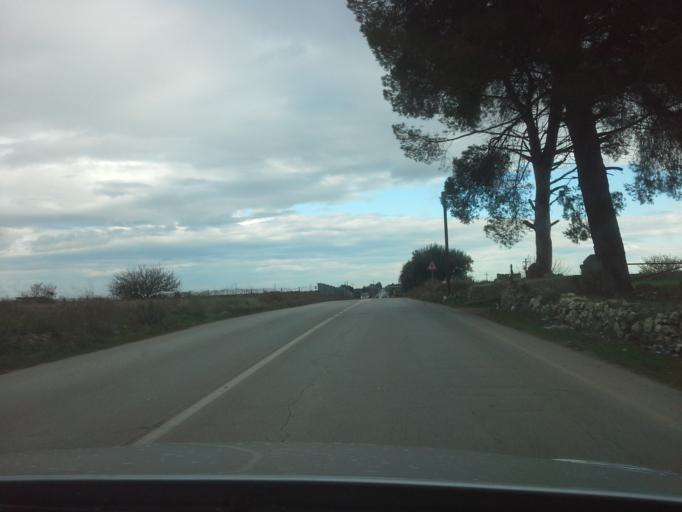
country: IT
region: Apulia
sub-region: Provincia di Bari
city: Adelfia
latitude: 41.0035
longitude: 16.8896
